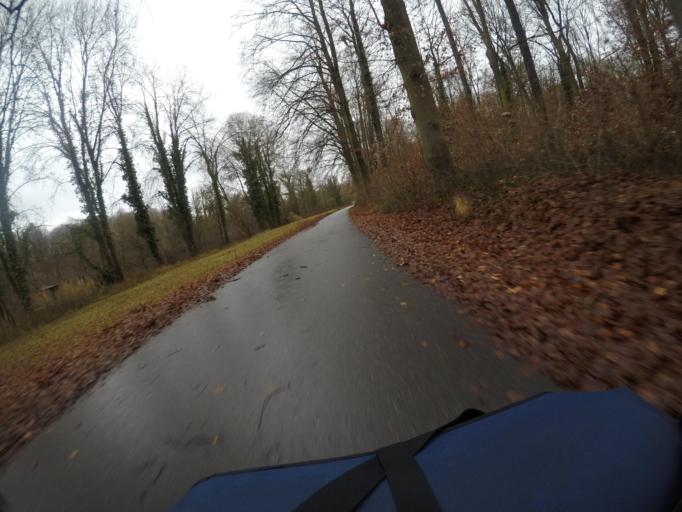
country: DE
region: Rheinland-Pfalz
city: Neupotz
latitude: 49.0761
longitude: 8.3135
